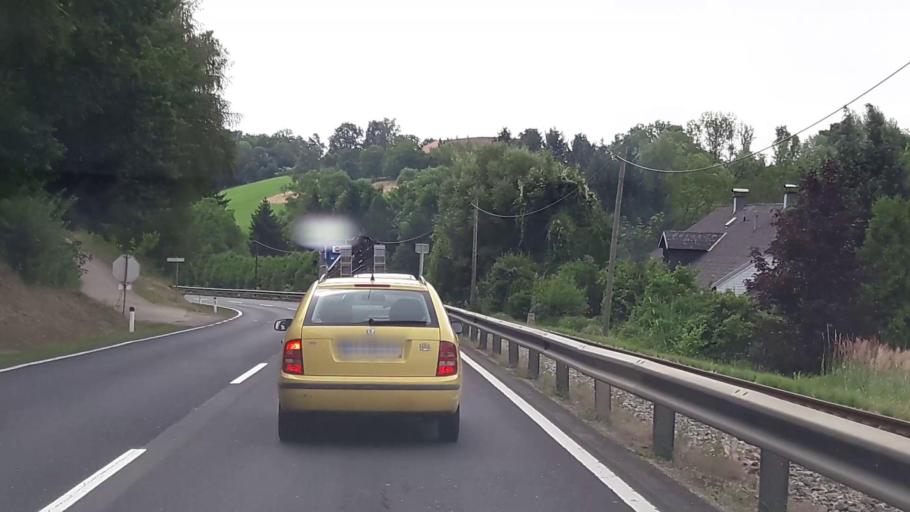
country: AT
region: Upper Austria
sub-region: Politischer Bezirk Urfahr-Umgebung
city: Sankt Gotthard im Muhlkreis
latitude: 48.3777
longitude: 14.0998
